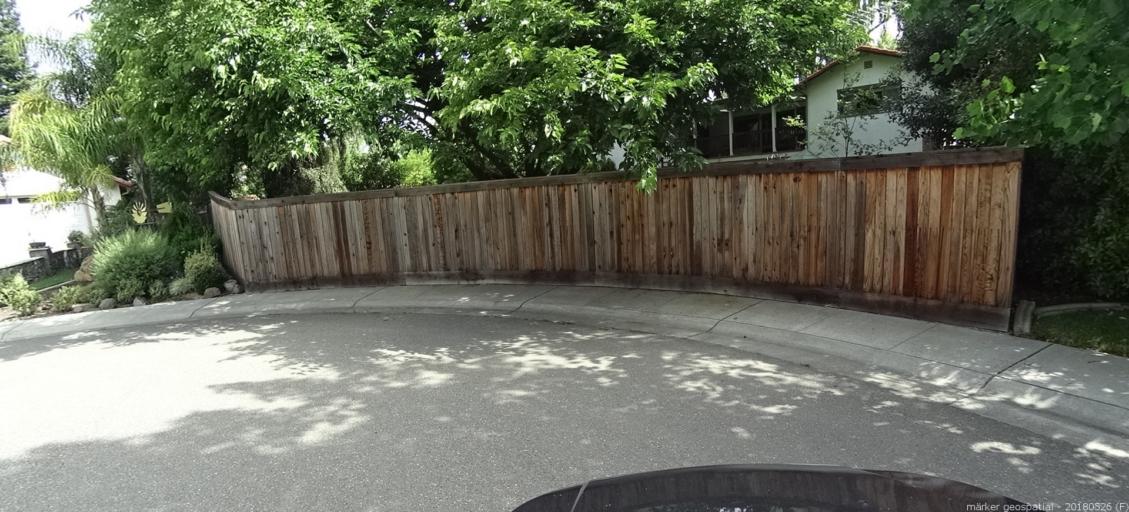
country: US
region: California
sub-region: Yolo County
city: West Sacramento
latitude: 38.6068
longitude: -121.5390
